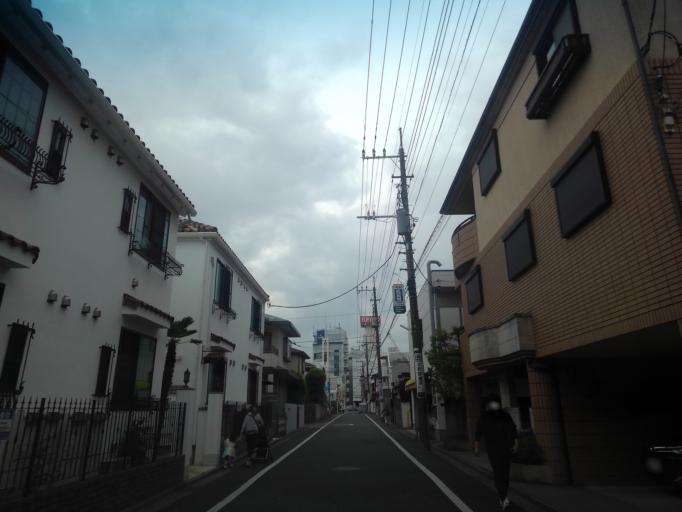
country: JP
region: Tokyo
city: Musashino
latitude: 35.7082
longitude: 139.5824
